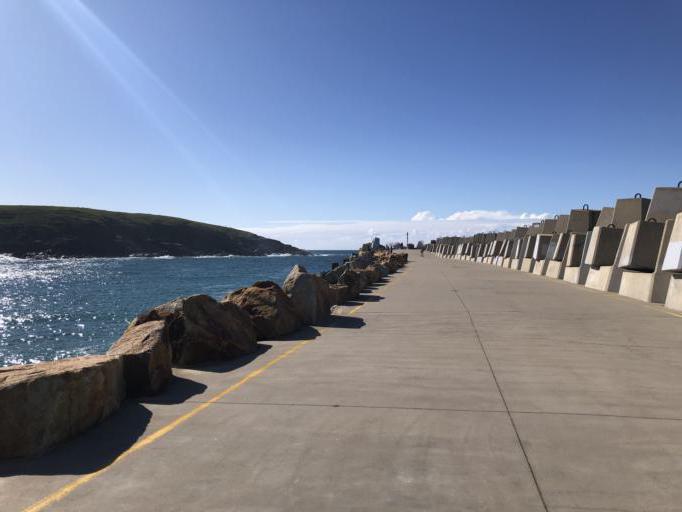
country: AU
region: New South Wales
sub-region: Coffs Harbour
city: Coffs Harbour
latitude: -30.3102
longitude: 153.1519
